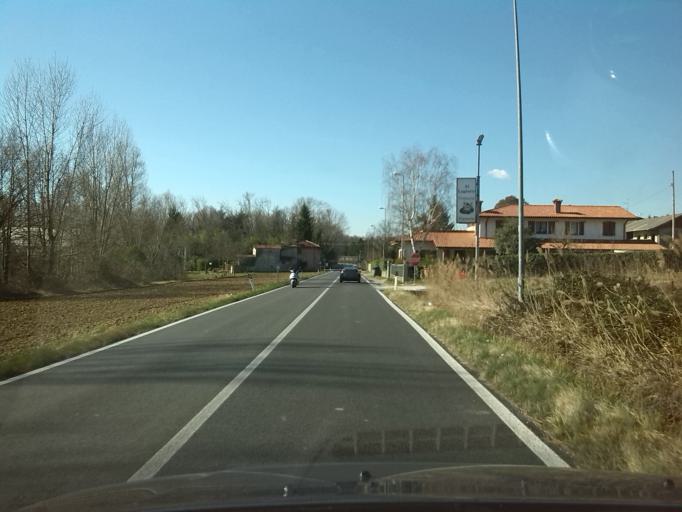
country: IT
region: Friuli Venezia Giulia
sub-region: Provincia di Udine
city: Moimacco
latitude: 46.1241
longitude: 13.3786
